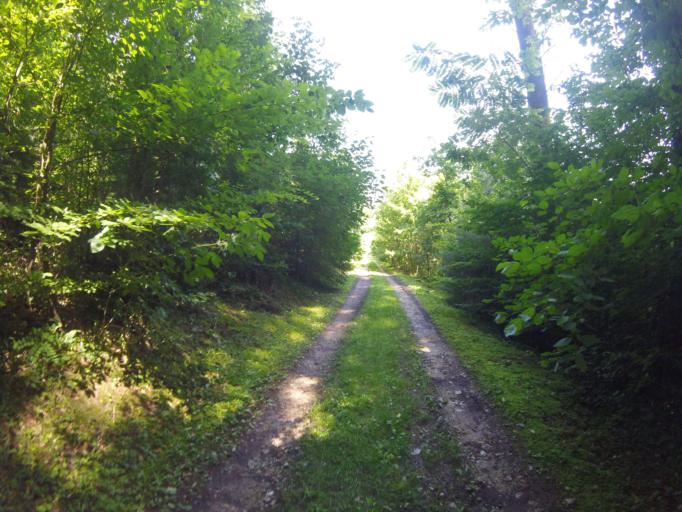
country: HU
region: Zala
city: Letenye
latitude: 46.5077
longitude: 16.6969
